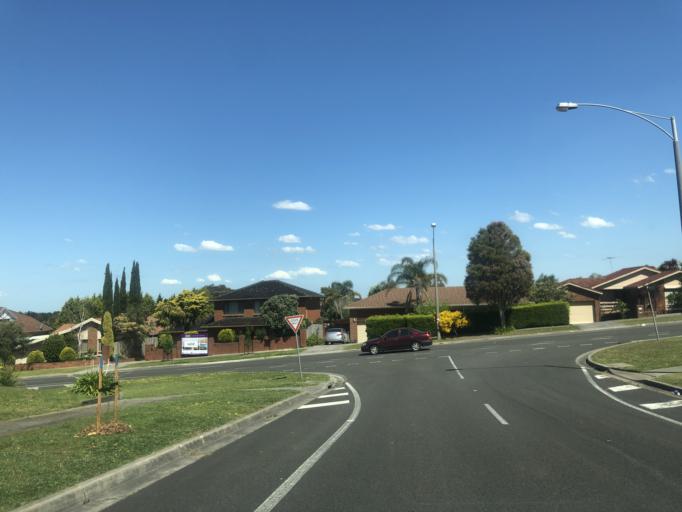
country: AU
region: Victoria
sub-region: Casey
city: Endeavour Hills
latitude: -37.9874
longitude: 145.2679
